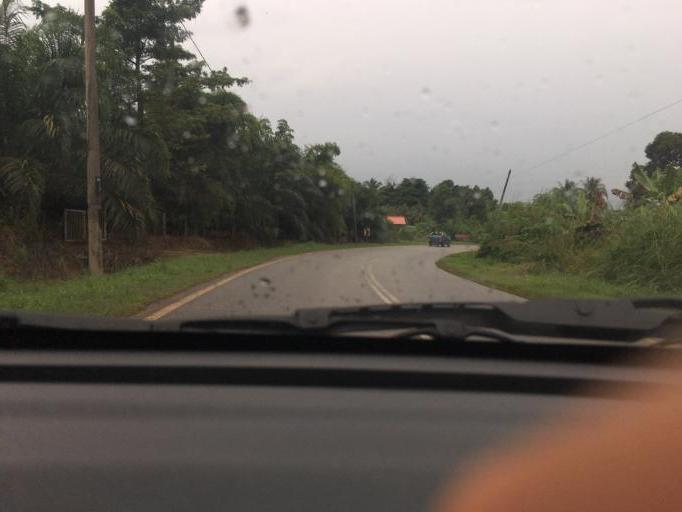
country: MY
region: Kedah
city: Bedong
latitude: 5.6970
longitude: 100.6332
